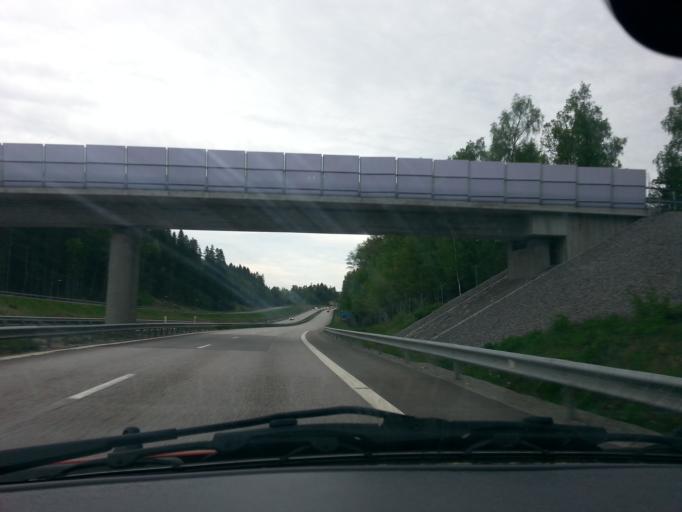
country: SE
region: Vaestra Goetaland
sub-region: Alingsas Kommun
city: Ingared
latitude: 57.8845
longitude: 12.4900
